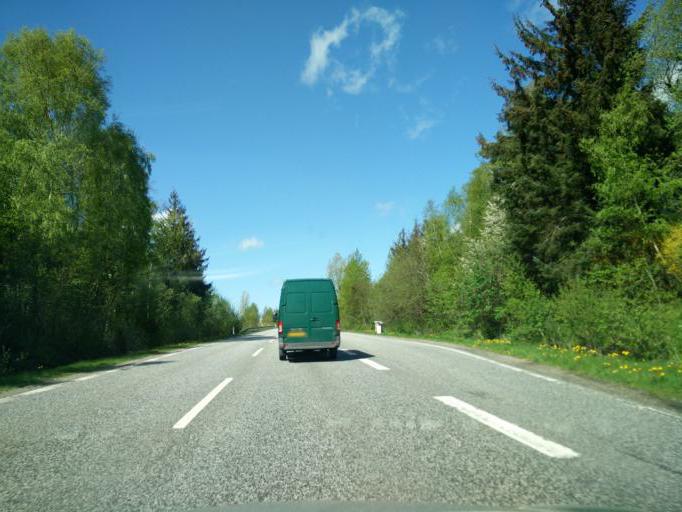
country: DK
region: Capital Region
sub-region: Hillerod Kommune
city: Hillerod
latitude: 55.9664
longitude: 12.2446
